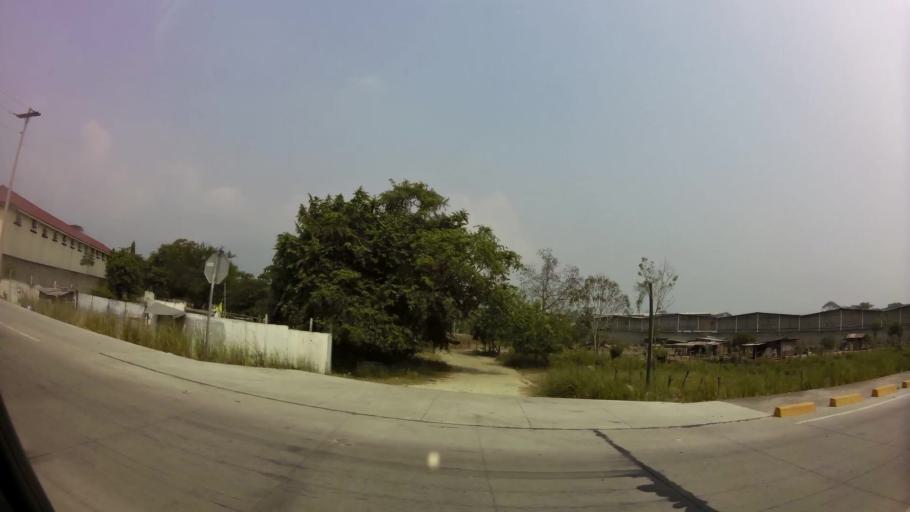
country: HN
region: Cortes
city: San Pedro Sula
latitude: 15.5381
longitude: -88.0014
